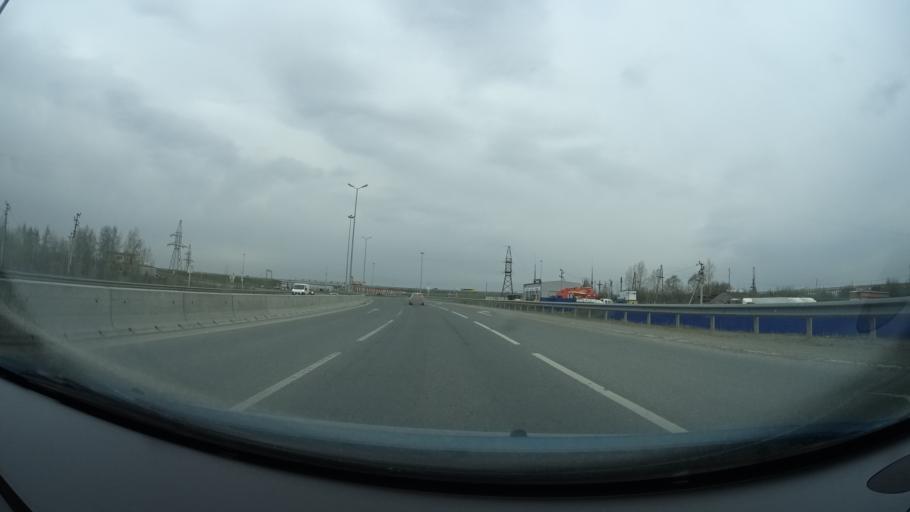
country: RU
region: Perm
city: Kondratovo
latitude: 58.0096
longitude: 56.0577
